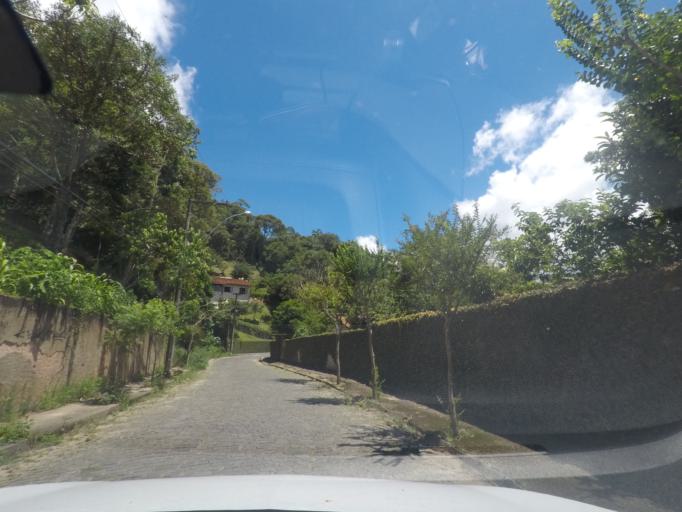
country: BR
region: Rio de Janeiro
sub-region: Teresopolis
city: Teresopolis
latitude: -22.4207
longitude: -42.9840
